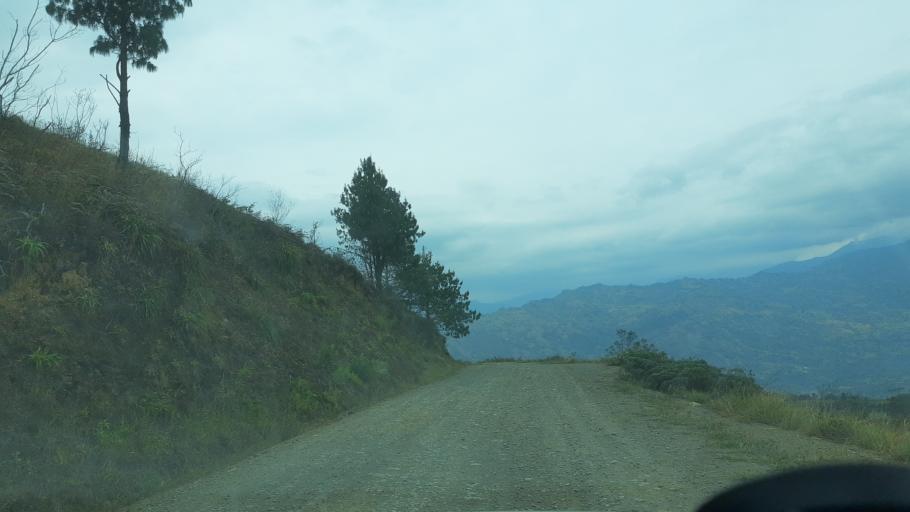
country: CO
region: Boyaca
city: Somondoco
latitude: 4.9829
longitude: -73.3754
